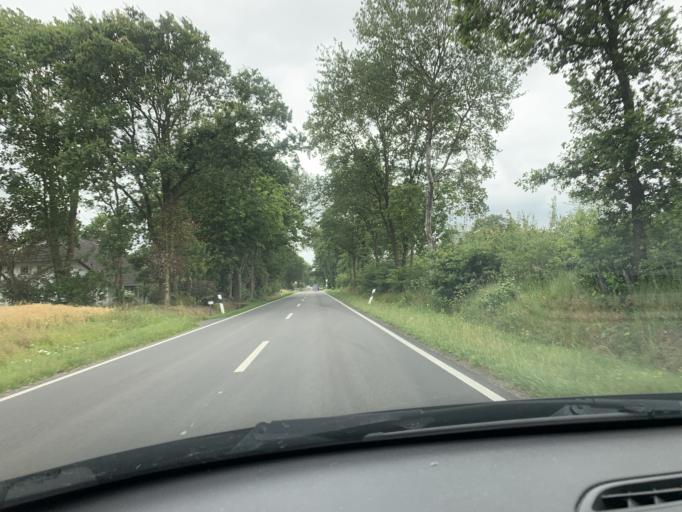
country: DE
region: Lower Saxony
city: Bad Zwischenahn
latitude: 53.2206
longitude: 7.9762
